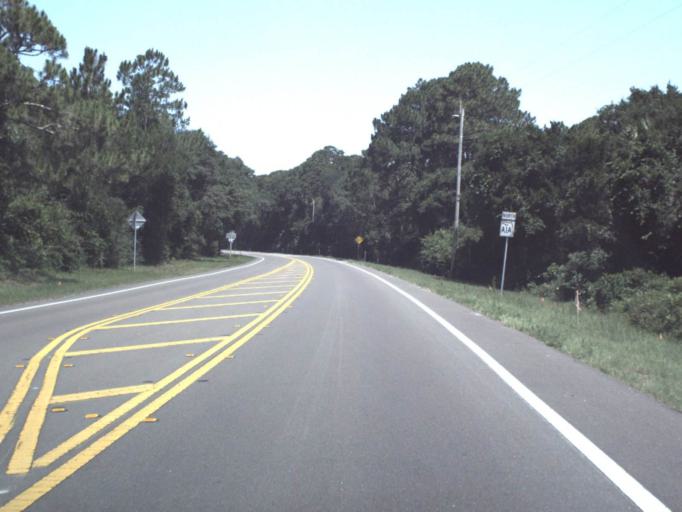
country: US
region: Florida
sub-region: Duval County
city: Atlantic Beach
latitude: 30.4587
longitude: -81.4190
